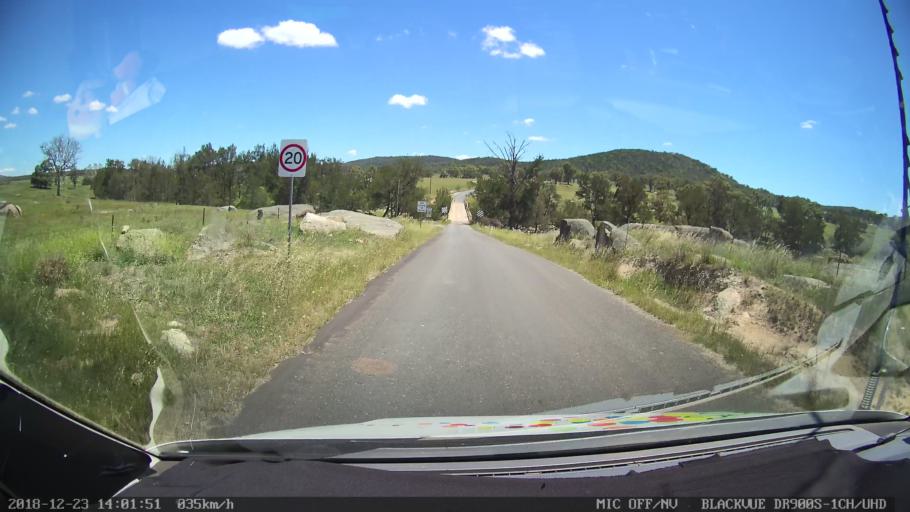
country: AU
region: New South Wales
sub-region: Tamworth Municipality
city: Manilla
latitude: -30.6223
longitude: 151.1102
